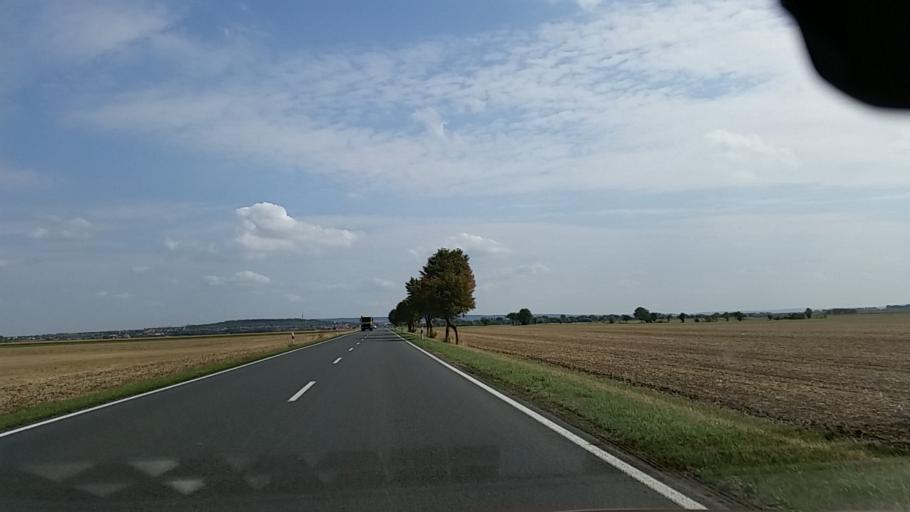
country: DE
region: Thuringia
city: Ringleben
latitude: 51.3676
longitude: 11.2341
